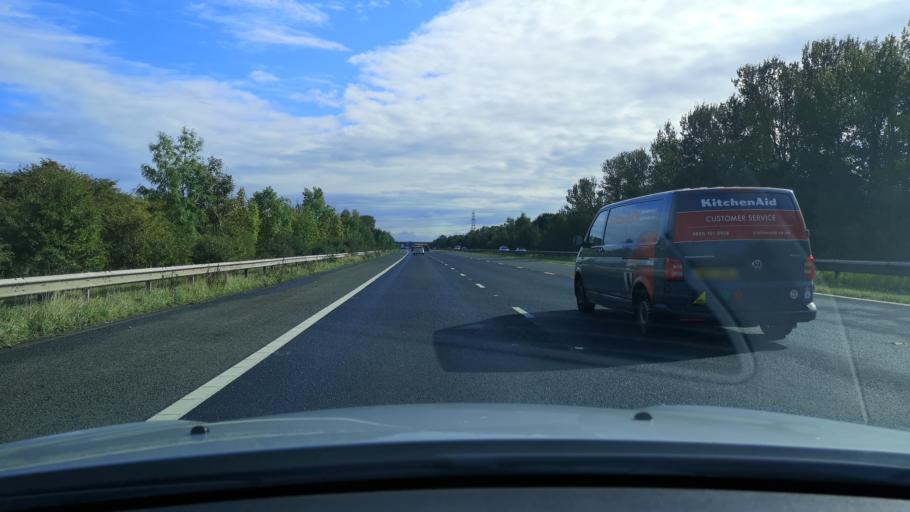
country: GB
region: England
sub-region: East Riding of Yorkshire
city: Pollington
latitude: 53.6823
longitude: -1.0668
